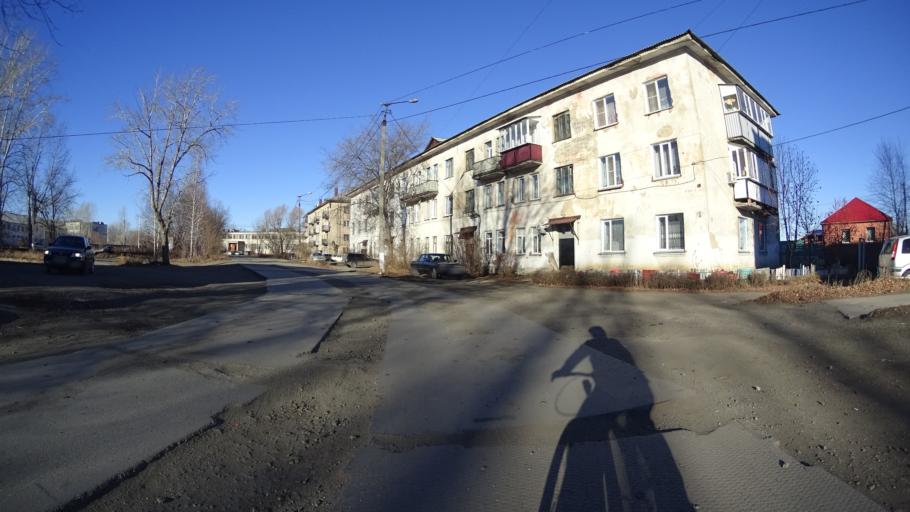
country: RU
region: Chelyabinsk
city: Troitsk
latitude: 54.1085
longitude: 61.5545
